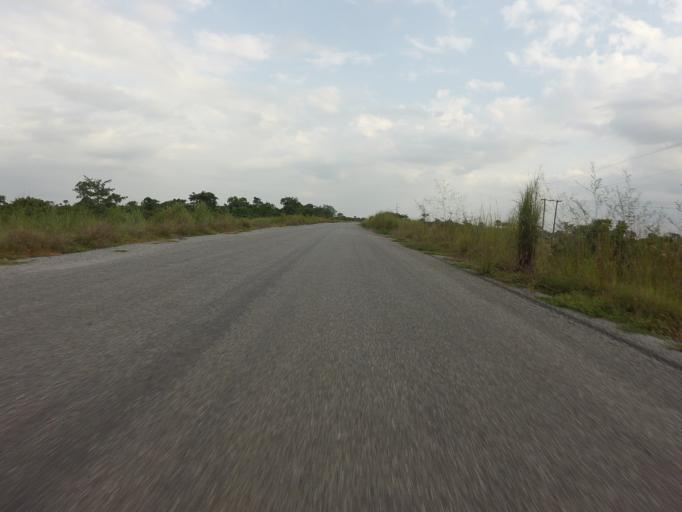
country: GH
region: Volta
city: Ho
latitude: 6.4056
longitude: 0.5238
